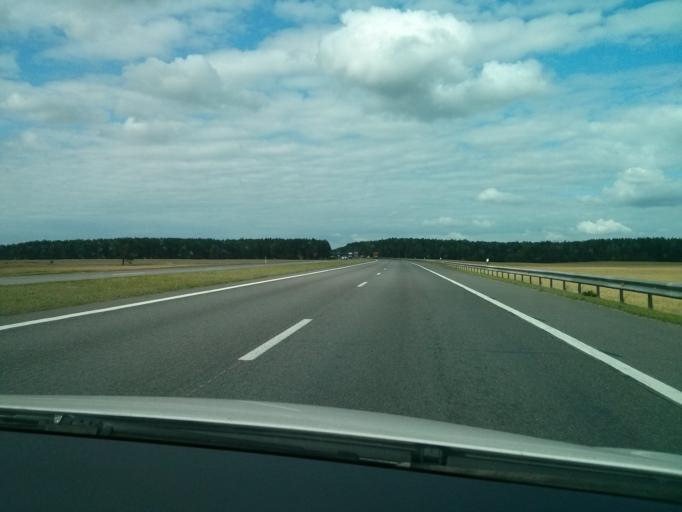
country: BY
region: Minsk
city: Zamostochcha
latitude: 53.8833
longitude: 27.9368
